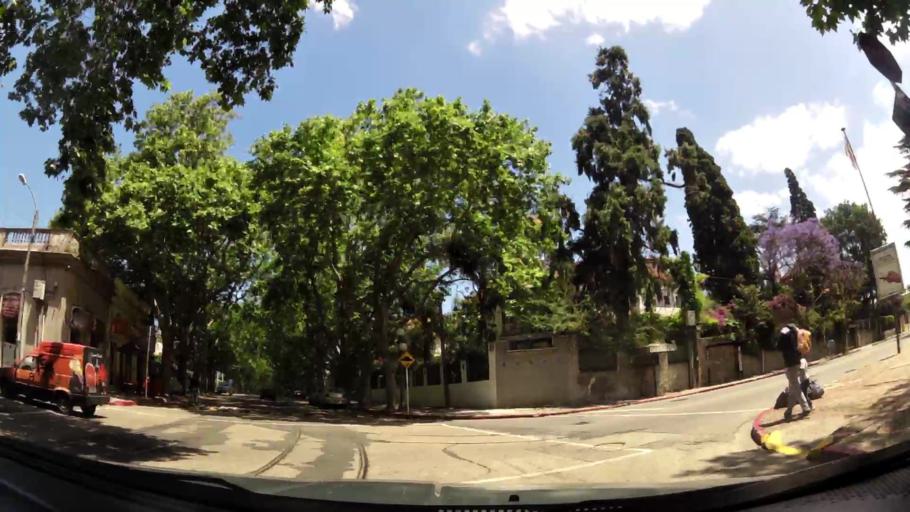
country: UY
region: Montevideo
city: Montevideo
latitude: -34.8638
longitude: -56.2027
